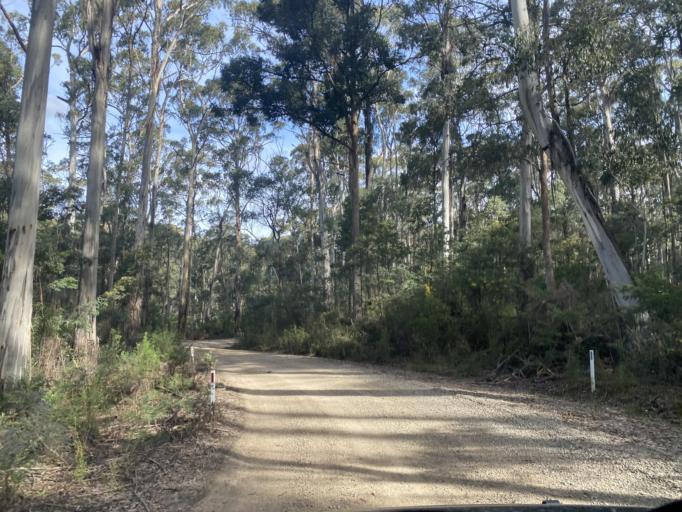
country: AU
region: Victoria
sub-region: Mansfield
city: Mansfield
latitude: -36.8542
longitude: 146.1918
